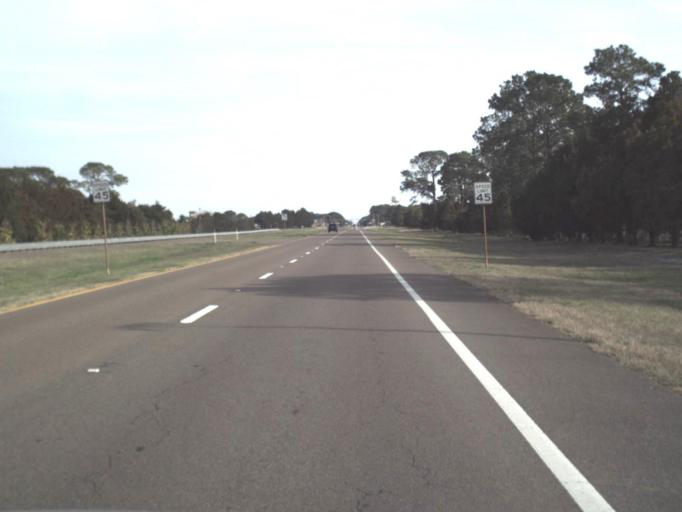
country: US
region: Florida
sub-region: Bay County
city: Tyndall Air Force Base
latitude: 30.0751
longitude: -85.5969
